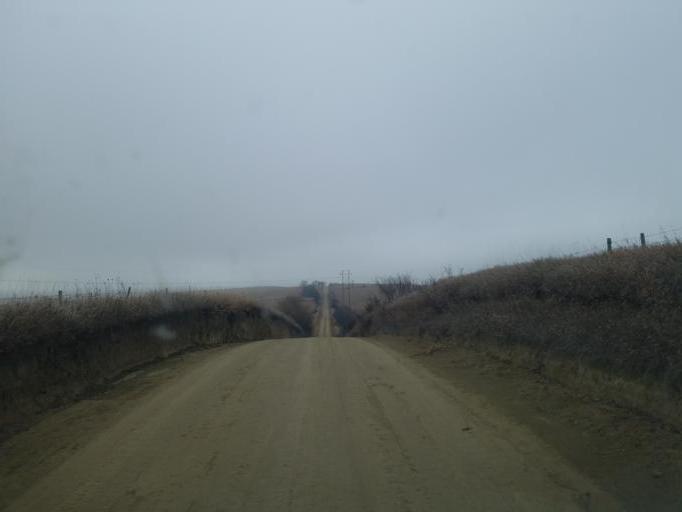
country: US
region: Nebraska
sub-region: Knox County
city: Center
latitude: 42.5722
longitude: -97.7984
